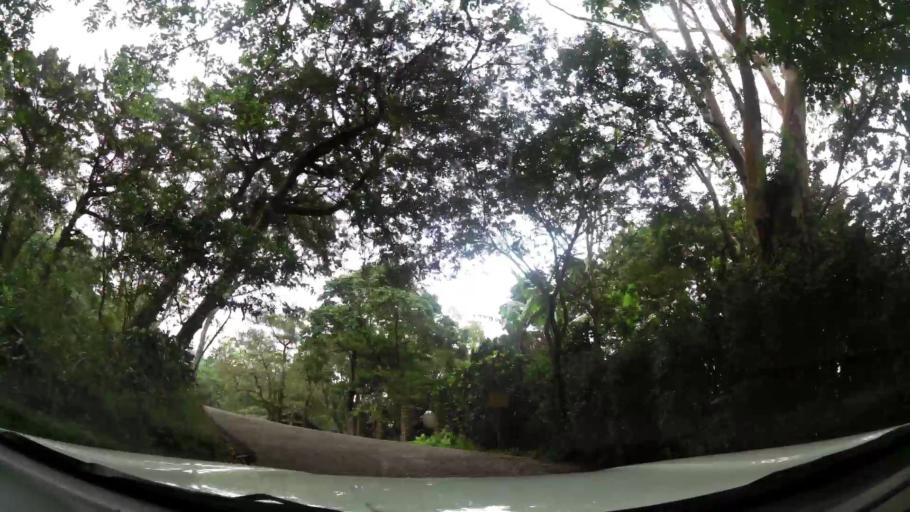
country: NI
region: Matagalpa
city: Matagalpa
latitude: 12.9967
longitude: -85.9092
